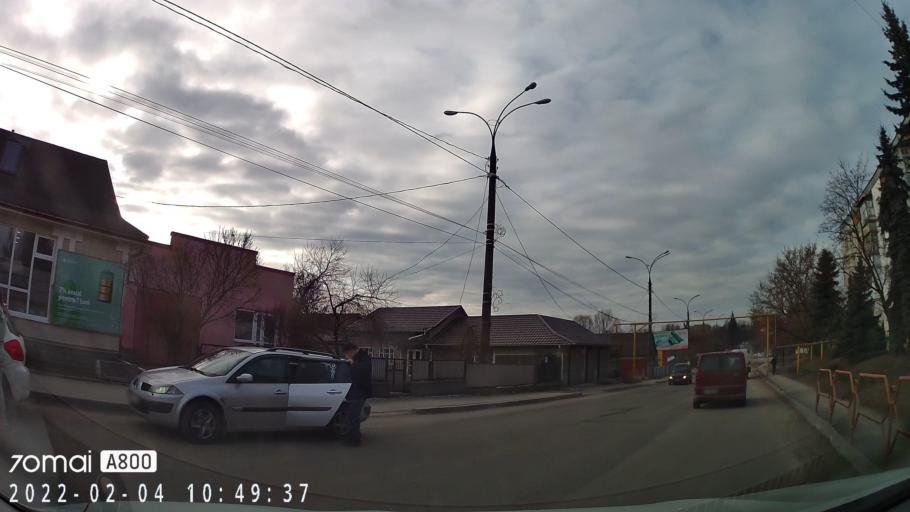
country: MD
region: Briceni
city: Briceni
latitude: 48.3577
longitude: 27.0900
